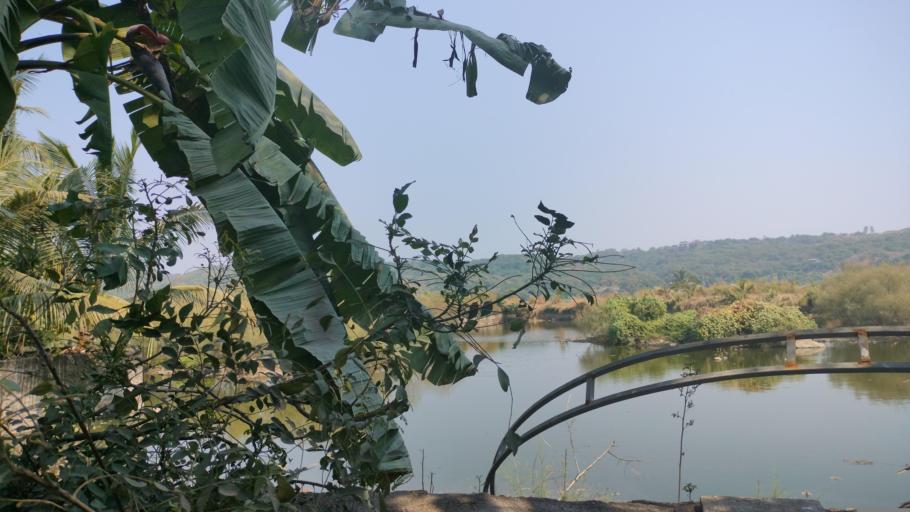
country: IN
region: Maharashtra
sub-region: Thane
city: Bhayandar
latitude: 19.2892
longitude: 72.7872
